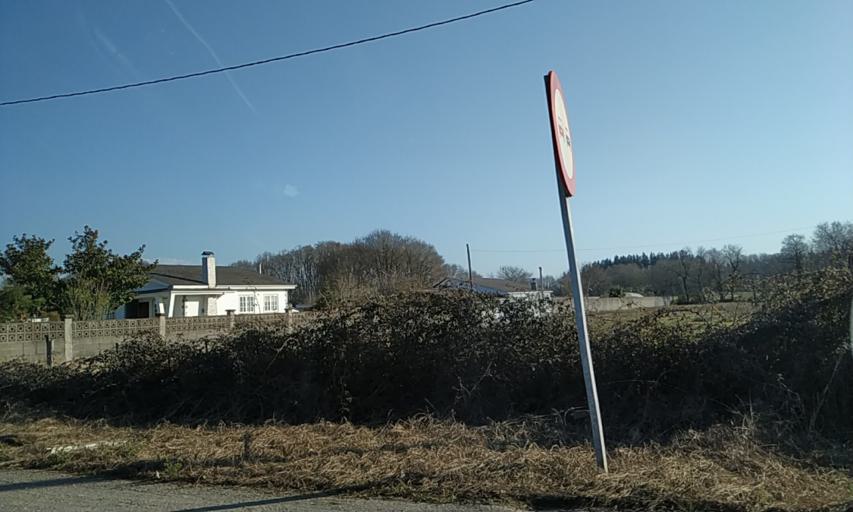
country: ES
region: Galicia
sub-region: Provincia de Lugo
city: Corgo
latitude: 42.9457
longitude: -7.4394
